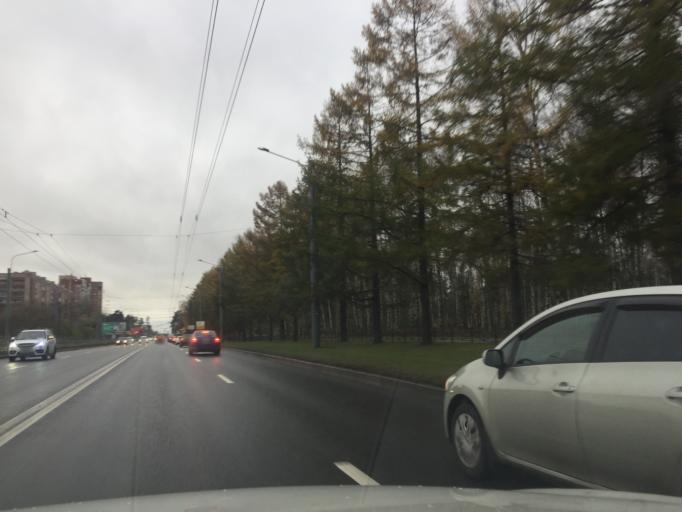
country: RU
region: St.-Petersburg
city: Sosnovka
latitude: 60.0147
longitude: 30.3570
